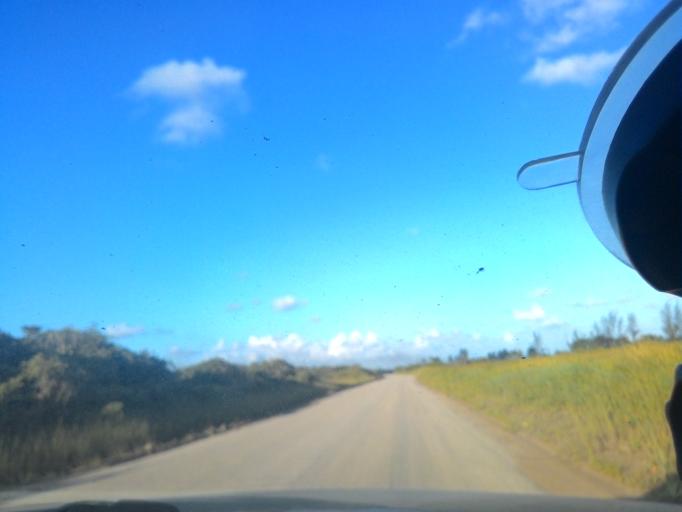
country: BR
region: Sao Paulo
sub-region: Iguape
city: Iguape
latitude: -24.8594
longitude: -47.7092
